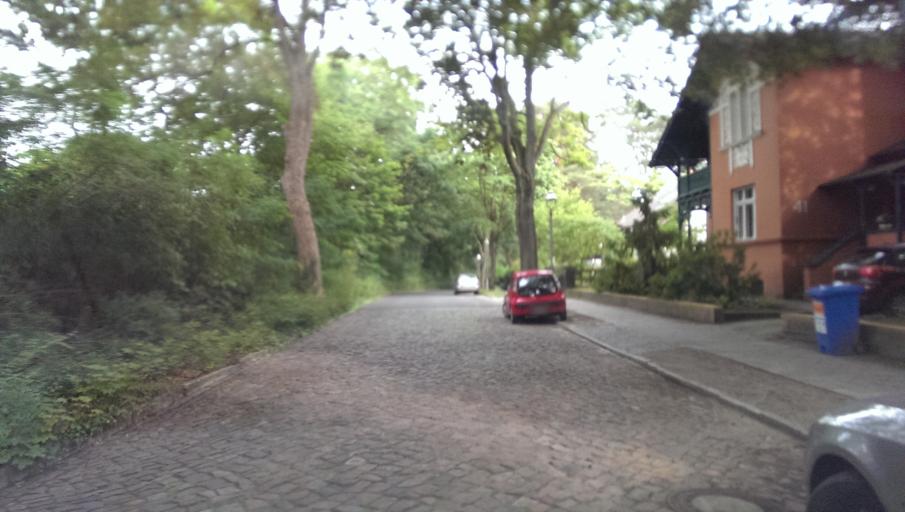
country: DE
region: Berlin
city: Nikolassee
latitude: 52.4404
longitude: 13.2232
